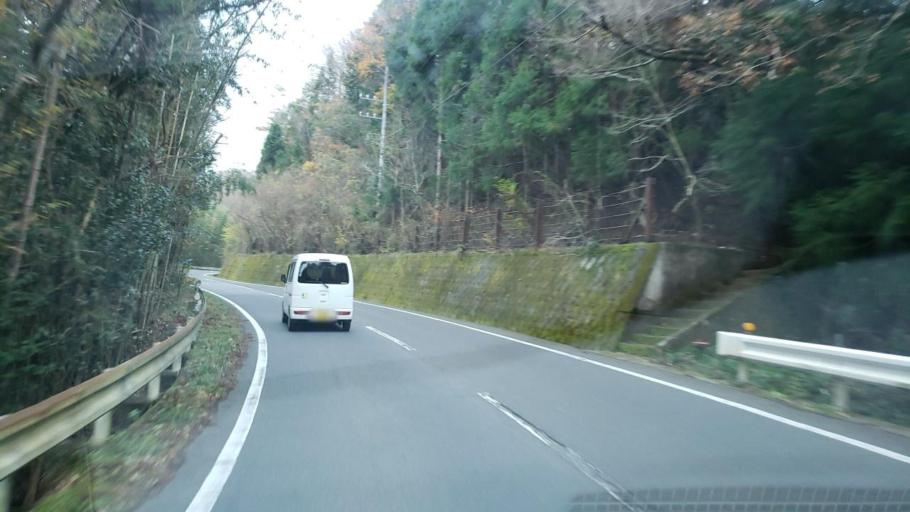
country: JP
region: Tokushima
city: Wakimachi
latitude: 34.1840
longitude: 134.1736
